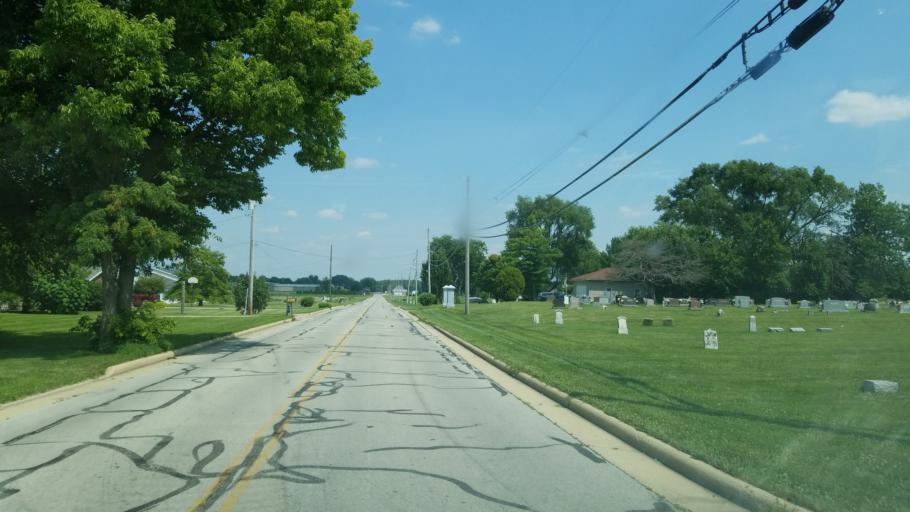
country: US
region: Ohio
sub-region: Seneca County
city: Tiffin
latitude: 41.1387
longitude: -83.1790
